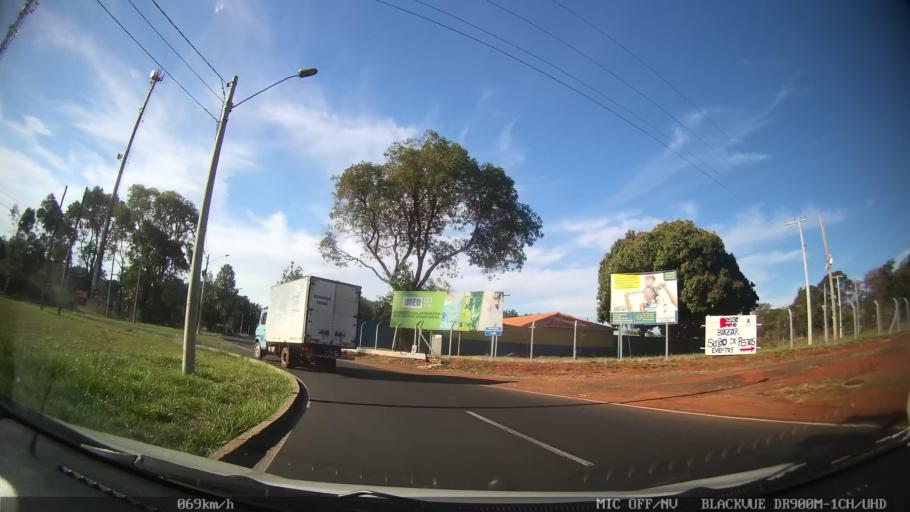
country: BR
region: Sao Paulo
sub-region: Araraquara
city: Araraquara
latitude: -21.7639
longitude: -48.1436
